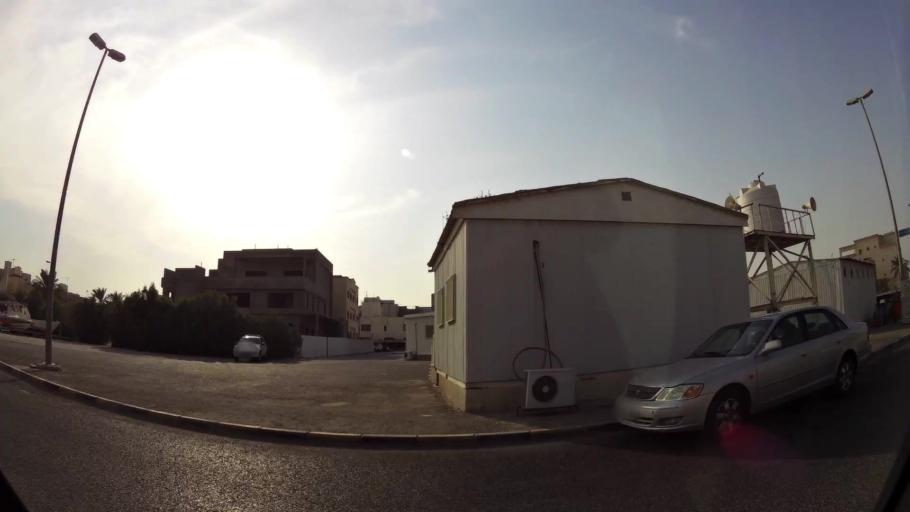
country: KW
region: Muhafazat Hawalli
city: Hawalli
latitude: 29.3245
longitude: 48.0085
